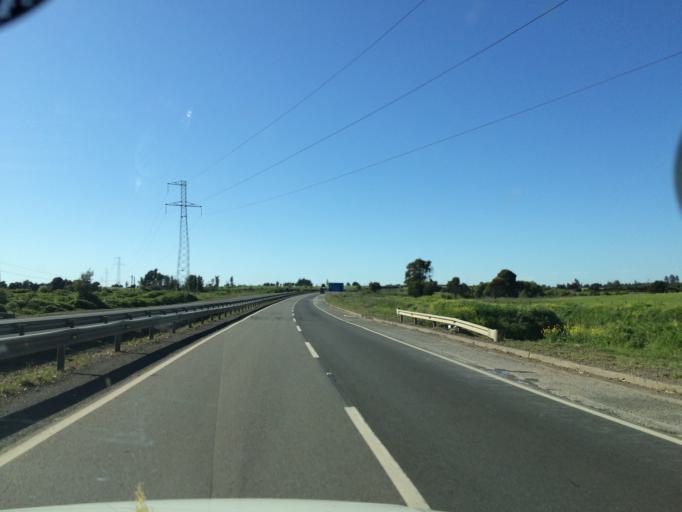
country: CL
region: Biobio
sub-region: Provincia de Biobio
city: Los Angeles
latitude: -37.4621
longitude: -72.4093
